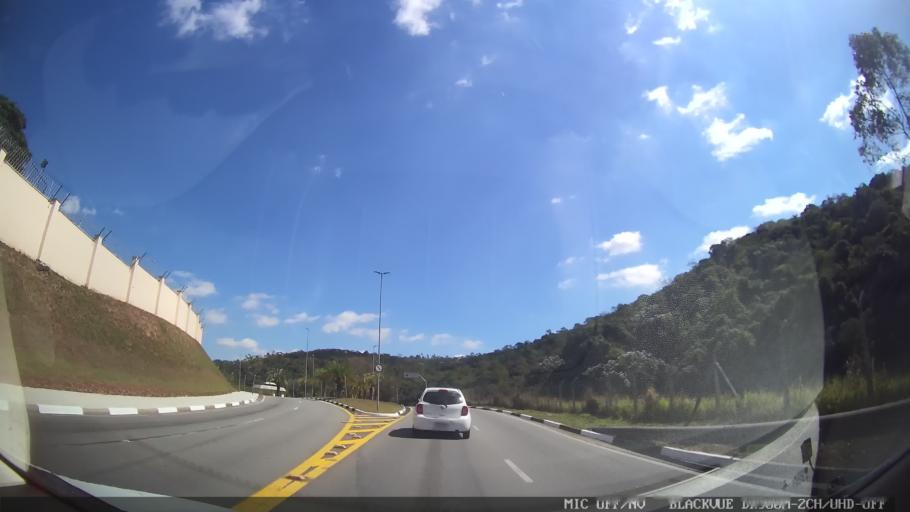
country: BR
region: Sao Paulo
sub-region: Santana De Parnaiba
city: Santana de Parnaiba
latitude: -23.4351
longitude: -46.8313
